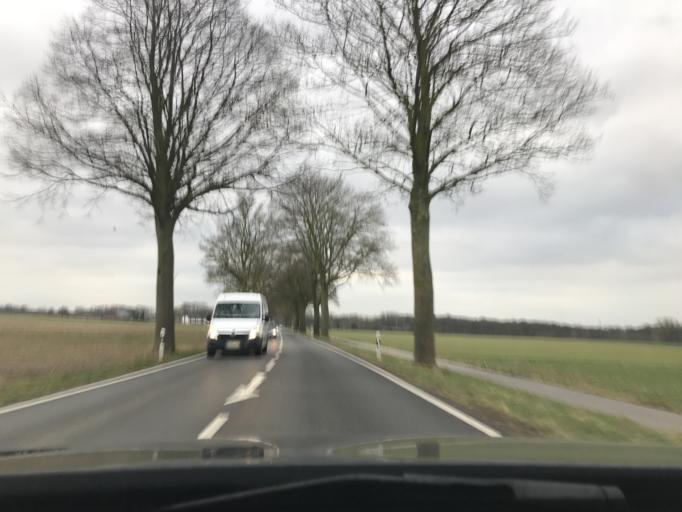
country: DE
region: North Rhine-Westphalia
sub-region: Regierungsbezirk Dusseldorf
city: Uedem
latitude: 51.6568
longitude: 6.2754
